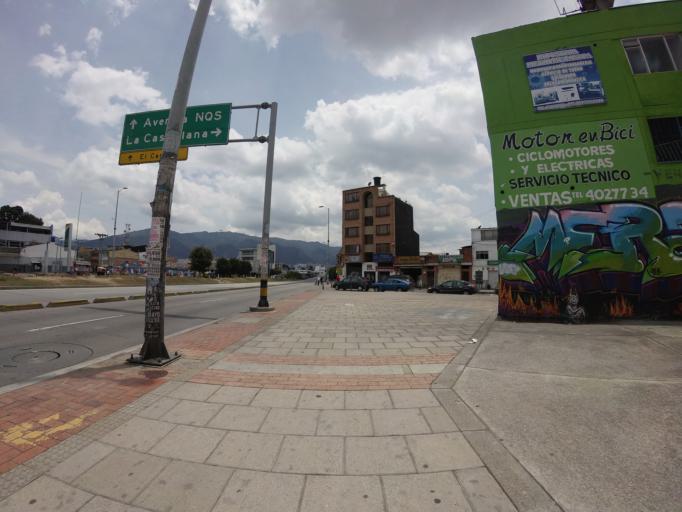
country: CO
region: Bogota D.C.
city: Barrio San Luis
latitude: 4.6865
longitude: -74.0644
